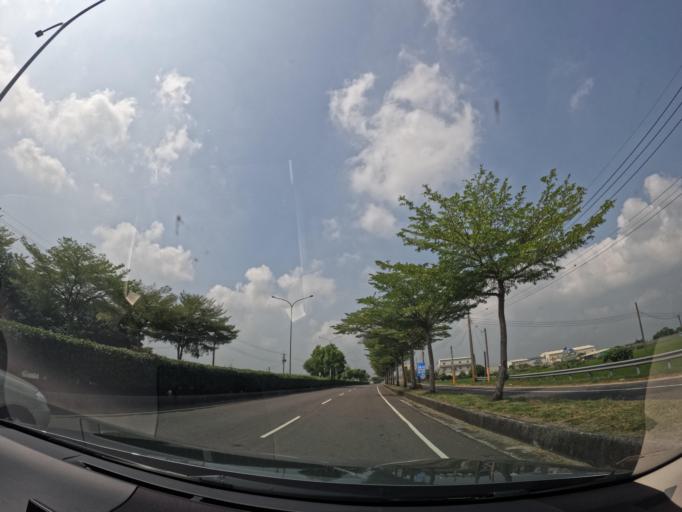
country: TW
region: Taiwan
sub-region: Yunlin
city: Douliu
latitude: 23.7072
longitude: 120.4892
